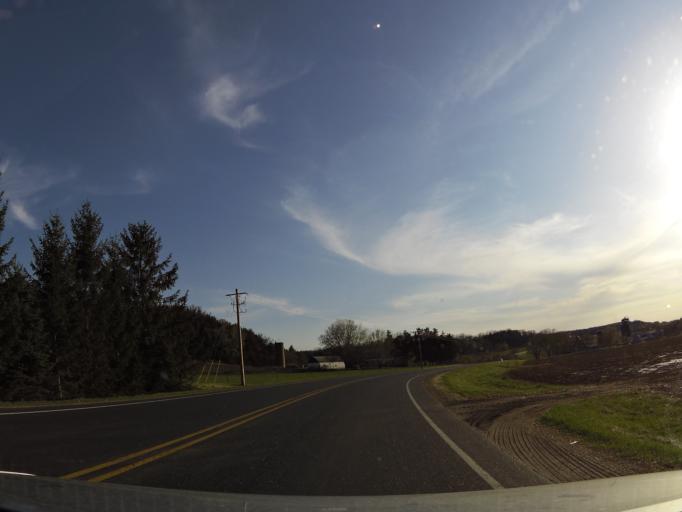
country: US
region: Wisconsin
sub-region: Pierce County
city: River Falls
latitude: 44.8310
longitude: -92.6608
